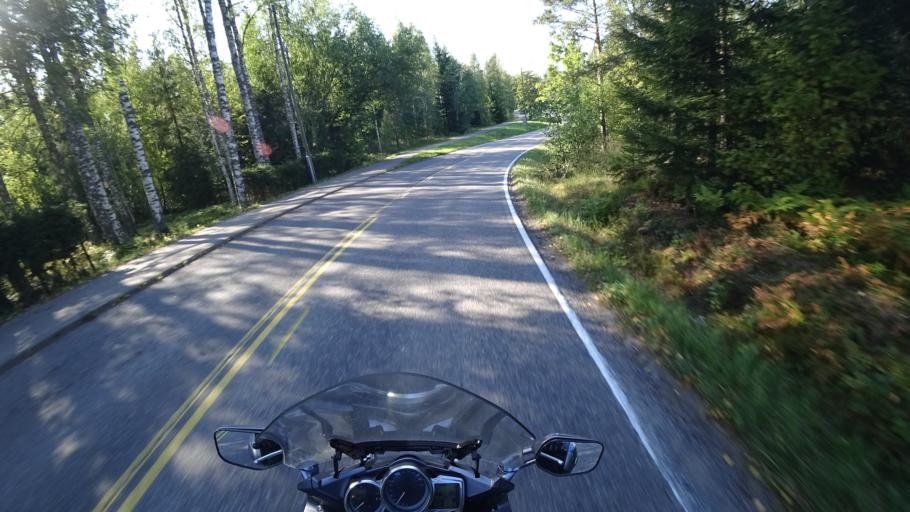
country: FI
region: Uusimaa
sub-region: Helsinki
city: Sammatti
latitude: 60.3168
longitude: 23.8303
